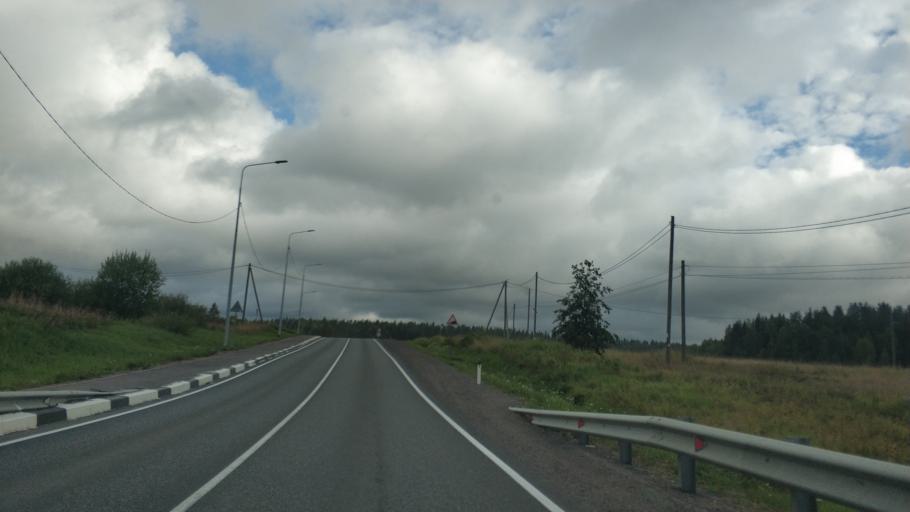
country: RU
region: Republic of Karelia
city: Khelyulya
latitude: 61.7580
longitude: 30.6572
